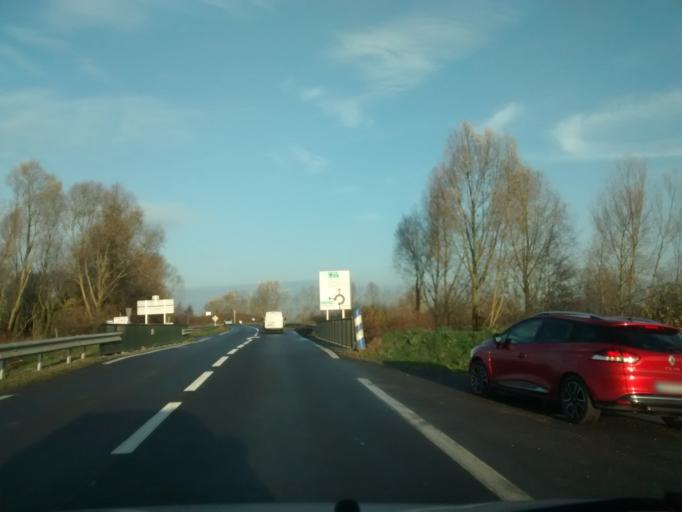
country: FR
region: Lower Normandy
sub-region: Departement de la Manche
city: Pontorson
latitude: 48.5589
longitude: -1.5289
